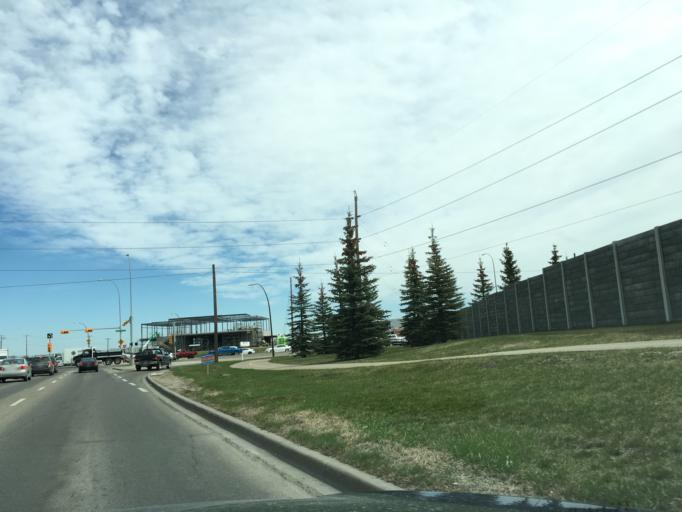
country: CA
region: Alberta
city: Calgary
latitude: 50.9804
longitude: -114.0512
